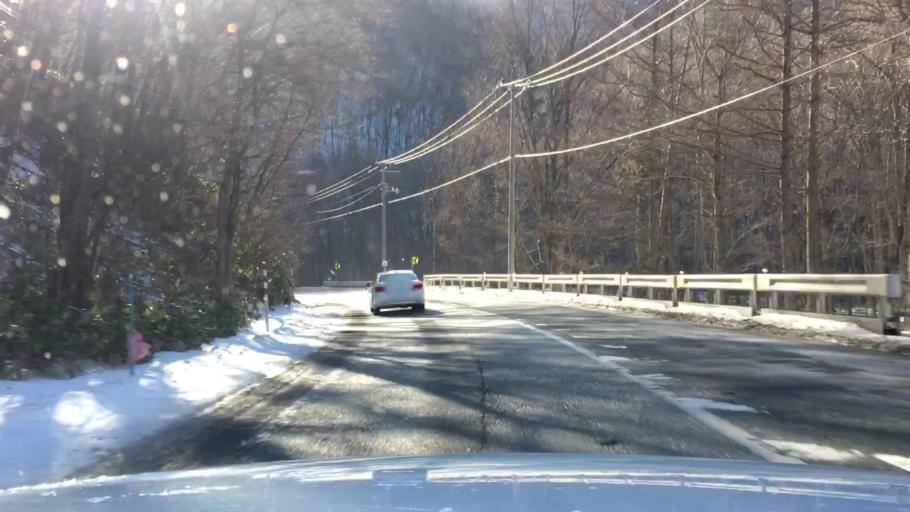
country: JP
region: Iwate
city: Morioka-shi
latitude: 39.6283
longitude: 141.4615
